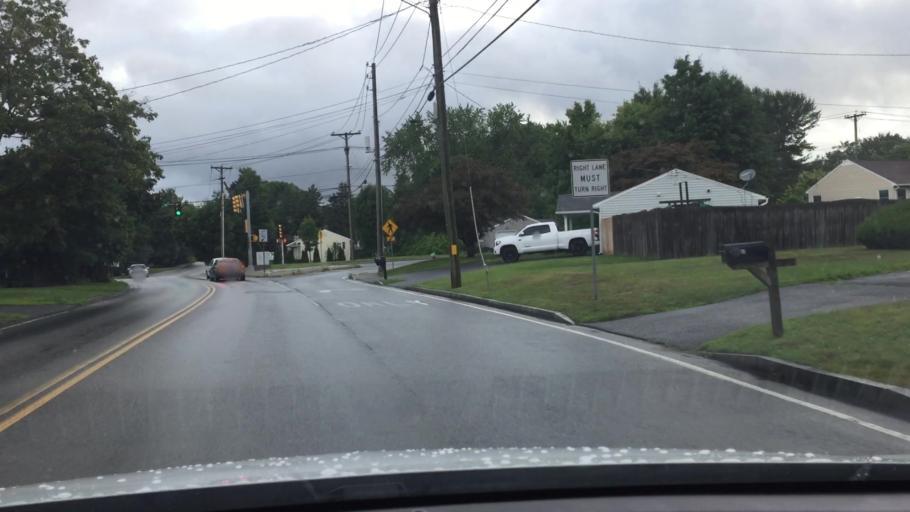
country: US
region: Massachusetts
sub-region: Berkshire County
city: Dalton
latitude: 42.4516
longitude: -73.1911
